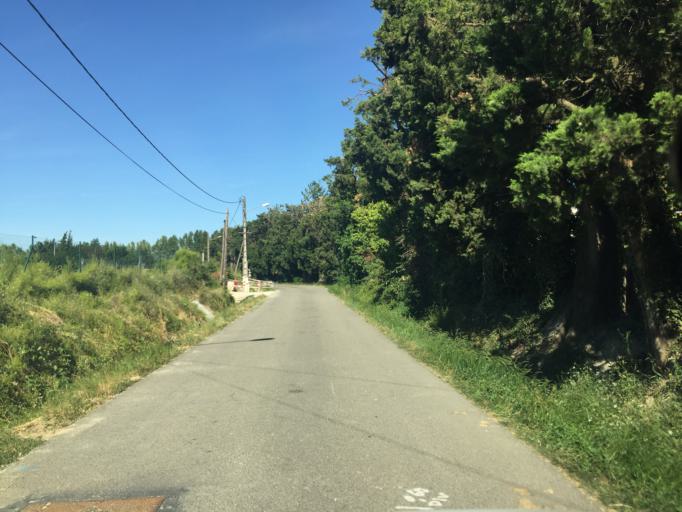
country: FR
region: Provence-Alpes-Cote d'Azur
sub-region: Departement du Vaucluse
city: Caderousse
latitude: 44.1042
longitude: 4.7522
